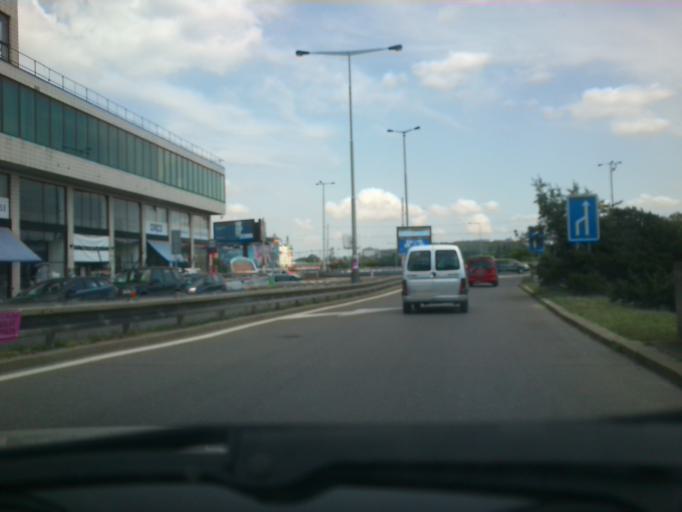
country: CZ
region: Praha
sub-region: Praha 8
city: Karlin
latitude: 50.0980
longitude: 14.4359
